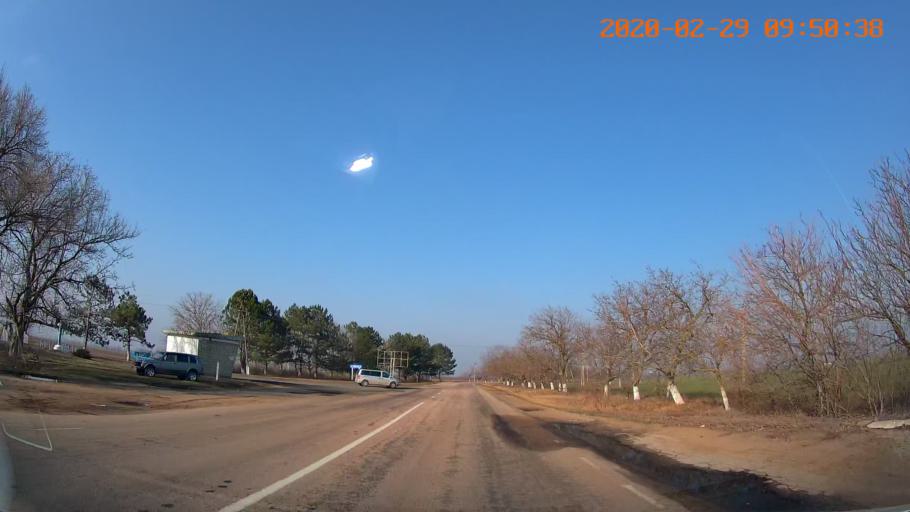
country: MD
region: Telenesti
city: Slobozia
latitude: 46.7028
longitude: 29.7521
